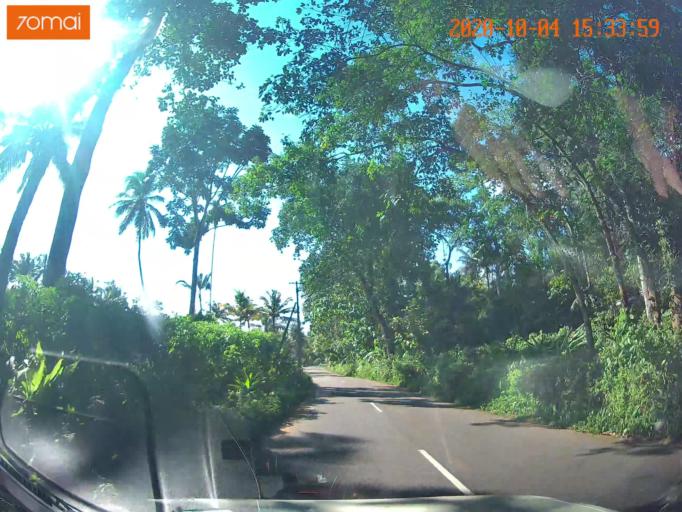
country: IN
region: Kerala
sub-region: Kottayam
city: Palackattumala
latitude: 9.7346
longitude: 76.6244
